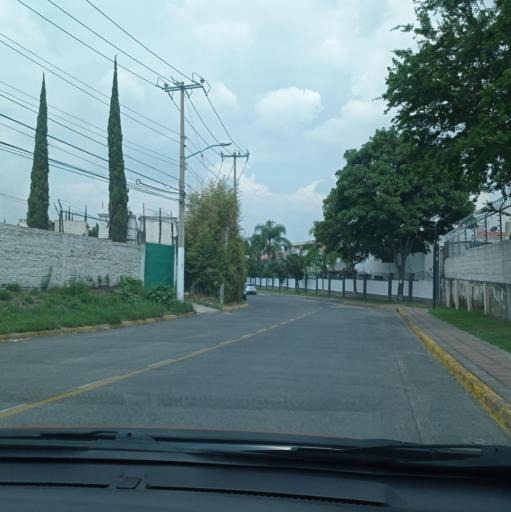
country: MX
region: Jalisco
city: Zapopan2
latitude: 20.6884
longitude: -103.4546
